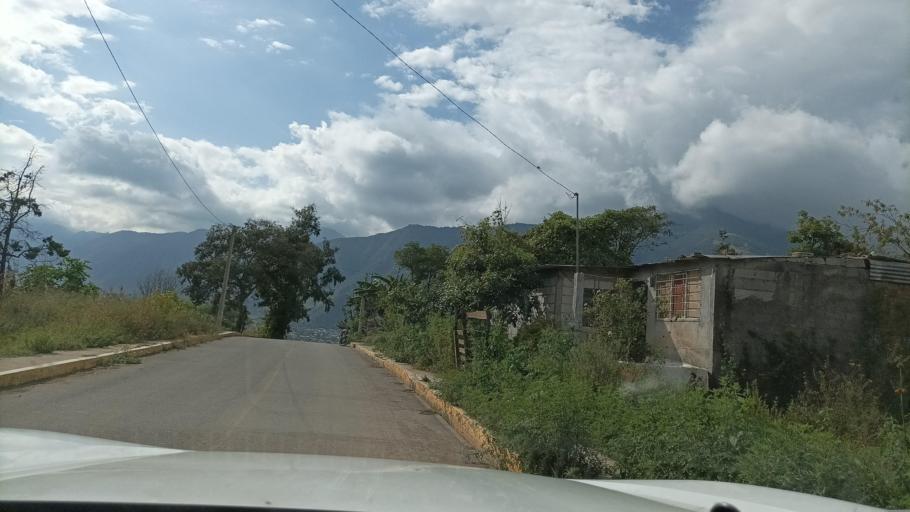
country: MX
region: Veracruz
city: Maltrata
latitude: 18.8164
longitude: -97.2580
